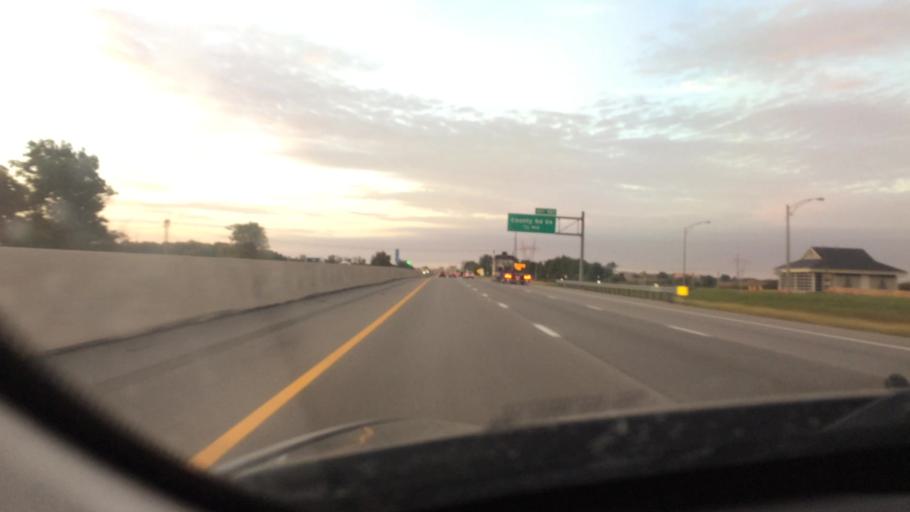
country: US
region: Ohio
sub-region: Hancock County
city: Findlay
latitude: 41.1033
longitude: -83.6596
